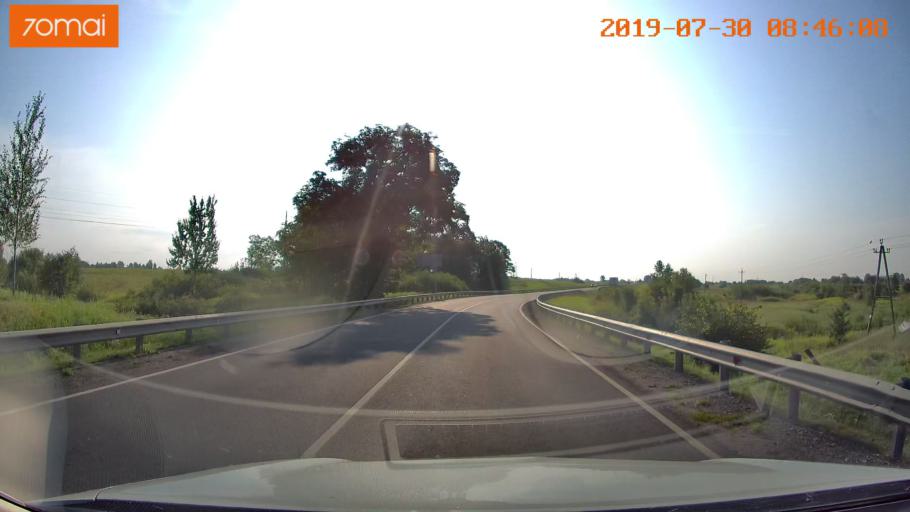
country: RU
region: Kaliningrad
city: Chernyakhovsk
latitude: 54.6249
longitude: 21.8785
